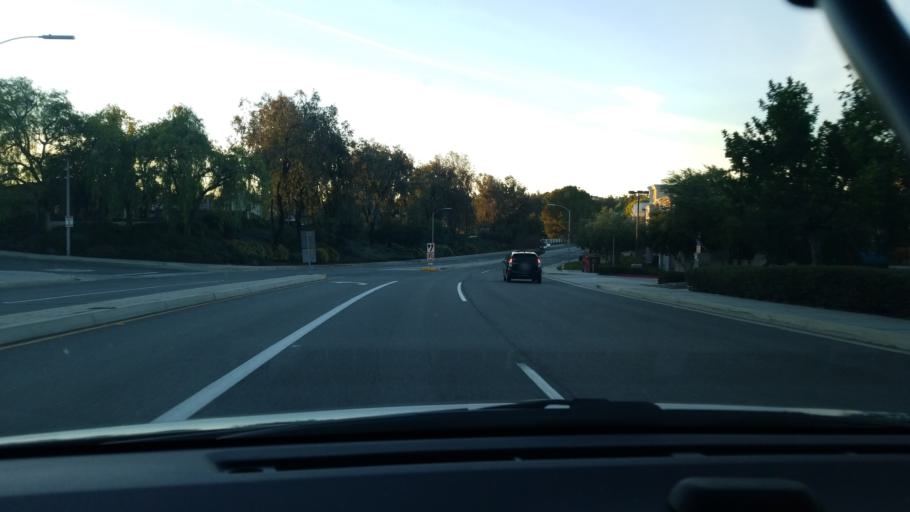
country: US
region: California
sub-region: Riverside County
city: Temecula
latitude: 33.5126
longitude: -117.1025
